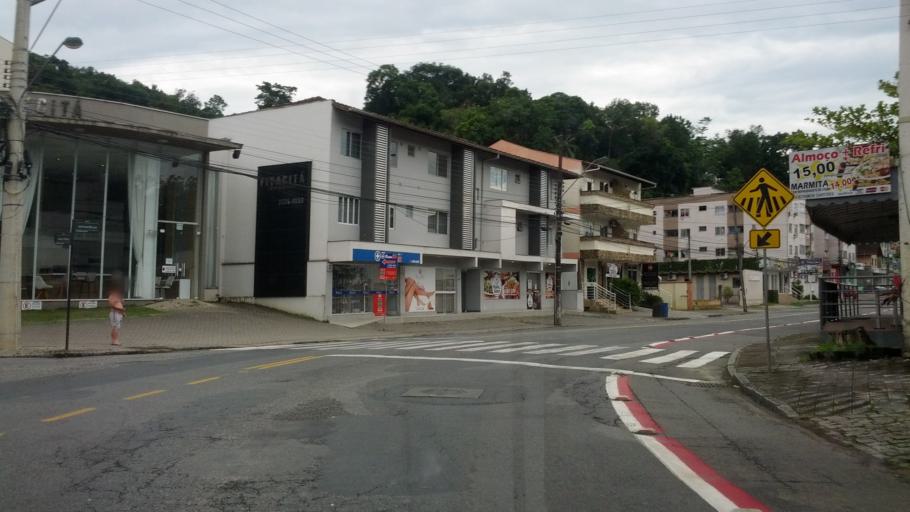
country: BR
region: Santa Catarina
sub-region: Blumenau
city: Blumenau
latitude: -26.8967
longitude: -49.0872
